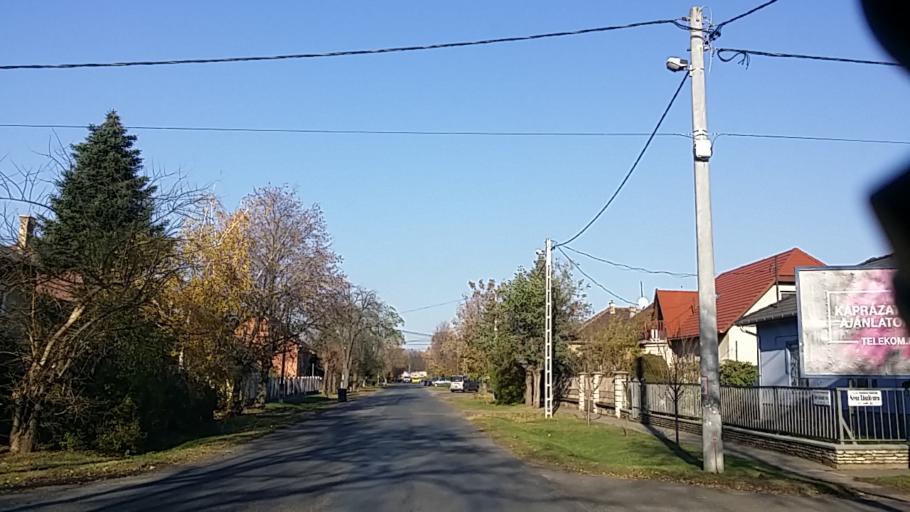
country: HU
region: Budapest
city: Budapest XVIII. keruelet
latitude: 47.4400
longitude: 19.2120
